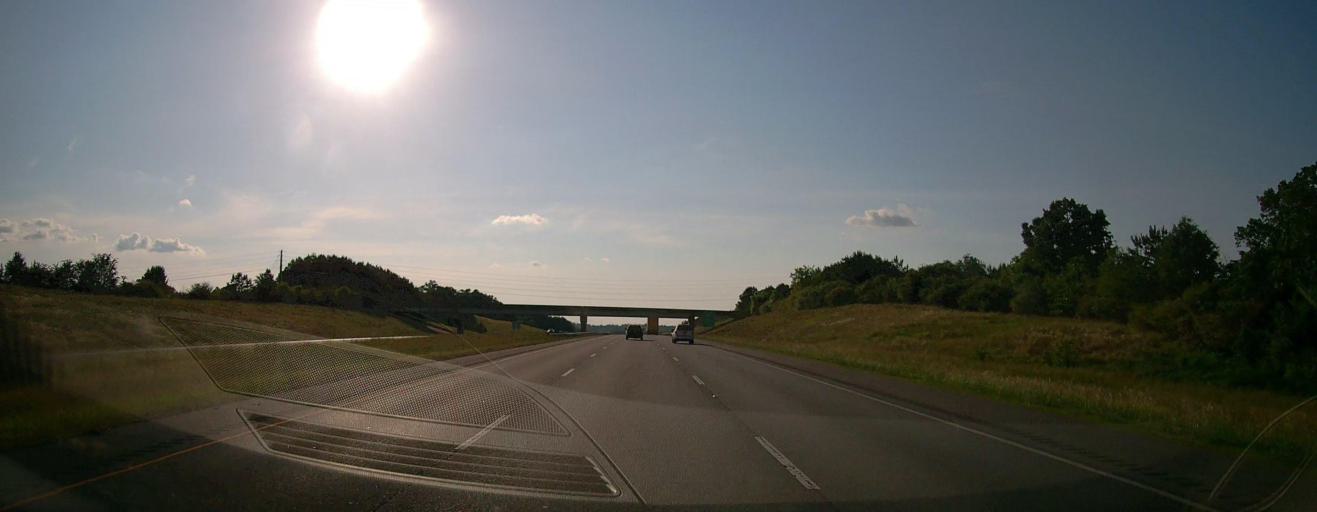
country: US
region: Alabama
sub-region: Walker County
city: Jasper
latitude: 33.7995
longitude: -87.2510
